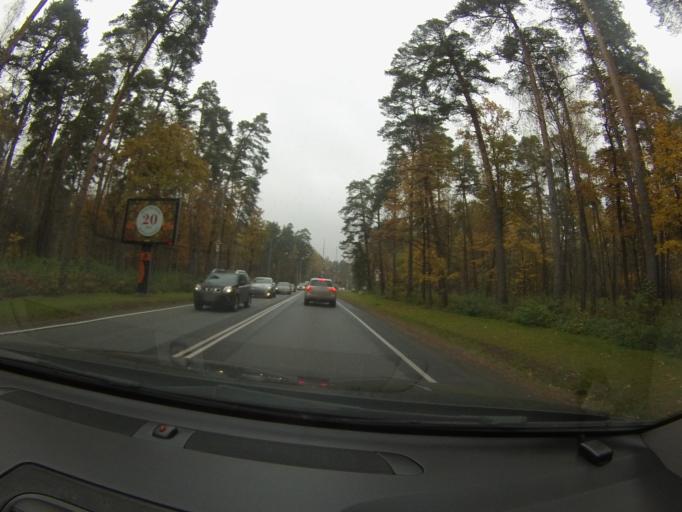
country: RU
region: Moscow
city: Rublevo
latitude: 55.7585
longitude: 37.3439
